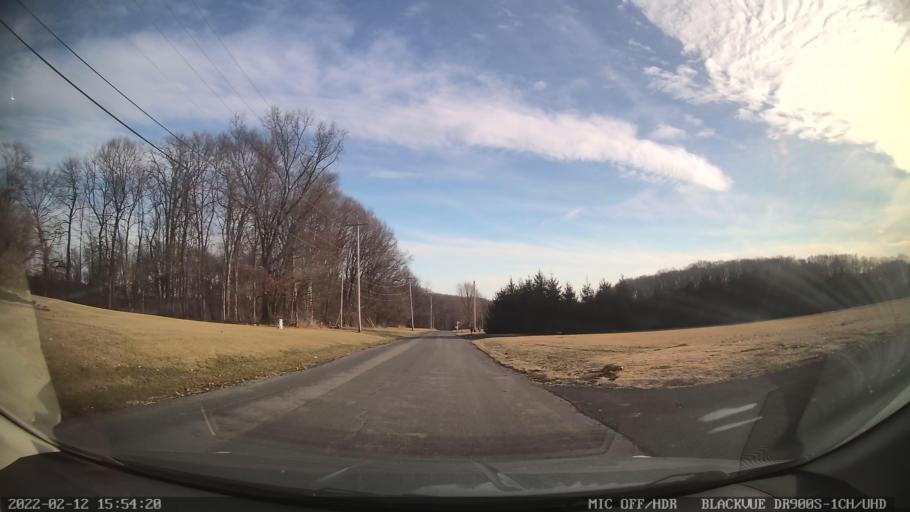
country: US
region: Pennsylvania
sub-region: Berks County
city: Kutztown
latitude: 40.5722
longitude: -75.7525
